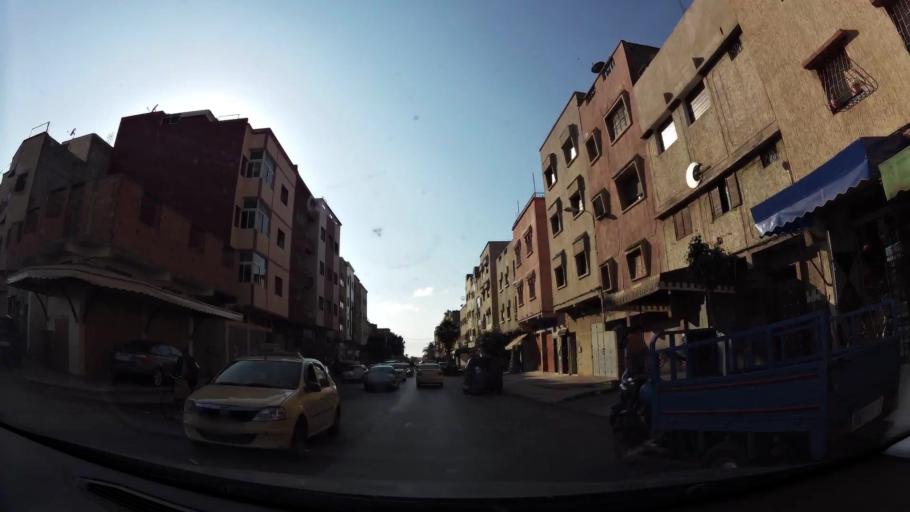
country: MA
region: Rabat-Sale-Zemmour-Zaer
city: Sale
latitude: 34.0581
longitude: -6.7883
